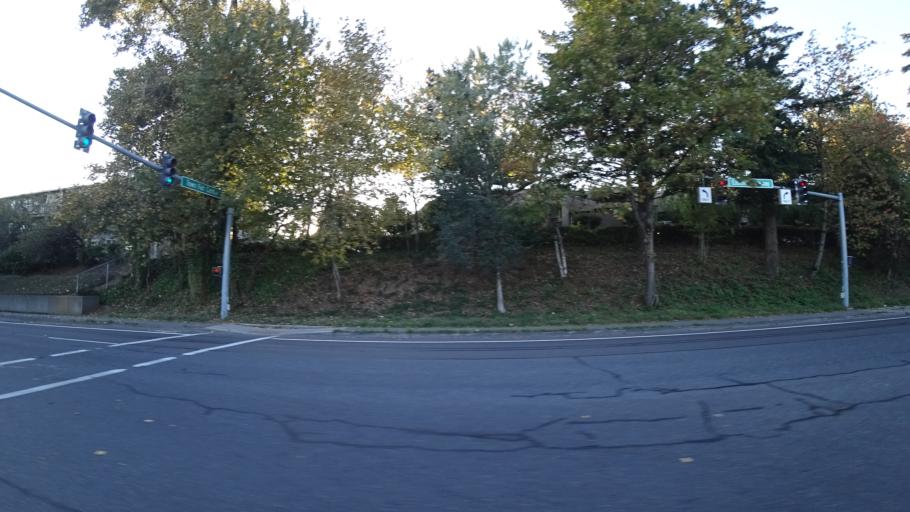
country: US
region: Oregon
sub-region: Multnomah County
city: Gresham
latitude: 45.5014
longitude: -122.4361
